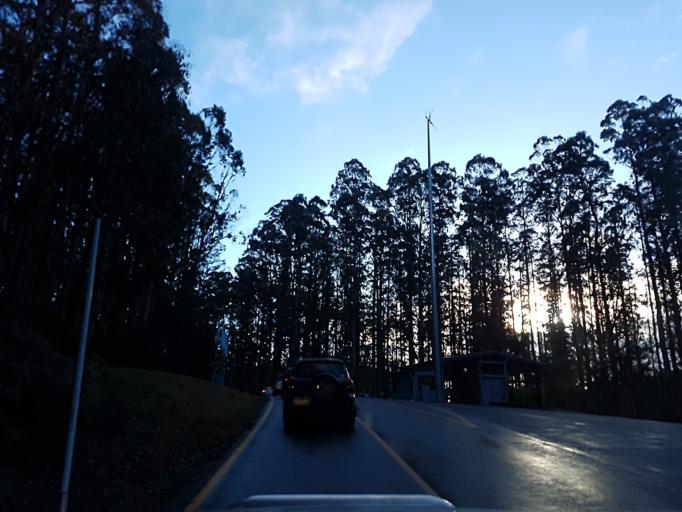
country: AU
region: Victoria
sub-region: Yarra Ranges
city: Millgrove
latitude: -37.5300
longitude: 145.8427
